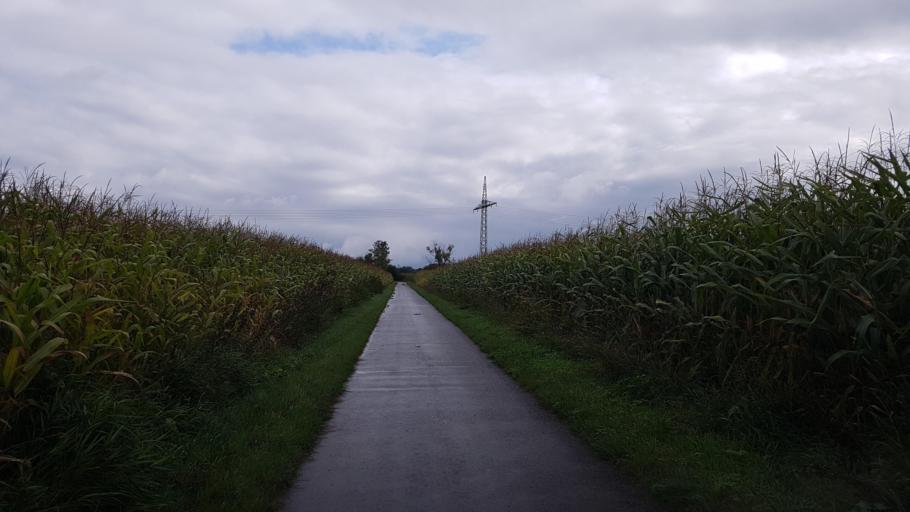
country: DE
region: Brandenburg
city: Tettau
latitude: 51.4617
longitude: 13.7243
